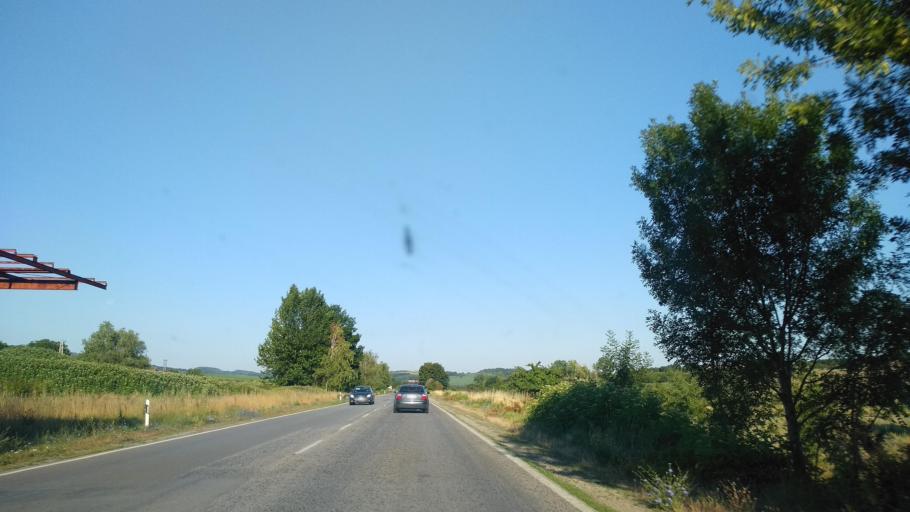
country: BG
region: Veliko Turnovo
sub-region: Obshtina Pavlikeni
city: Byala Cherkva
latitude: 43.0840
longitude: 25.3590
